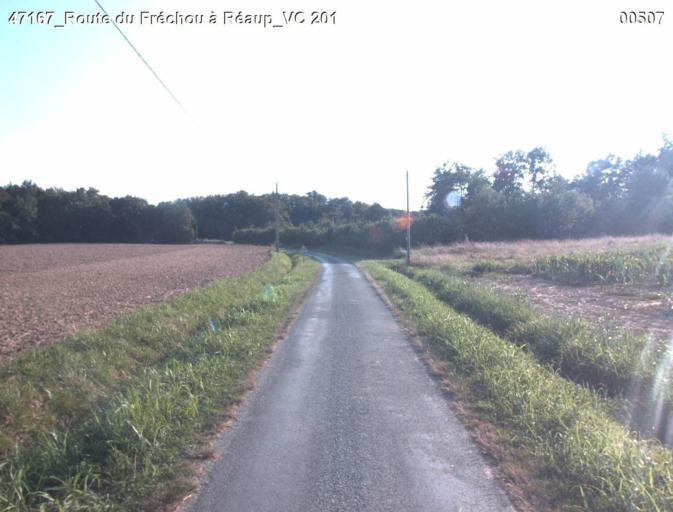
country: FR
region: Aquitaine
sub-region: Departement du Lot-et-Garonne
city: Mezin
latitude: 44.0794
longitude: 0.3052
